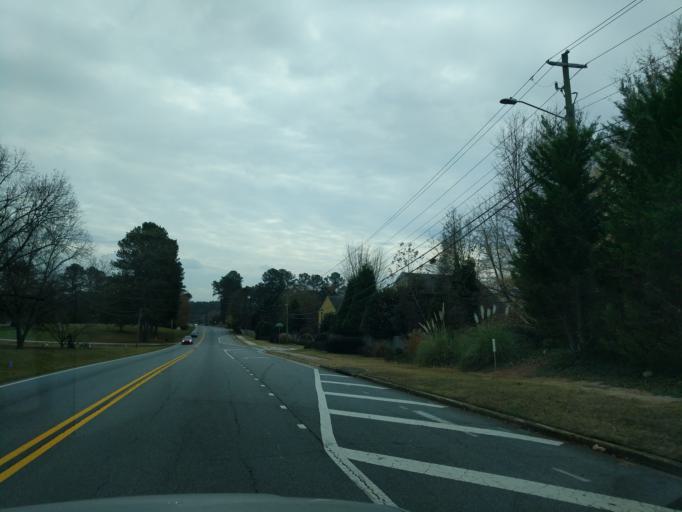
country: US
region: Georgia
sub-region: Gwinnett County
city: Duluth
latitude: 33.9951
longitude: -84.1360
